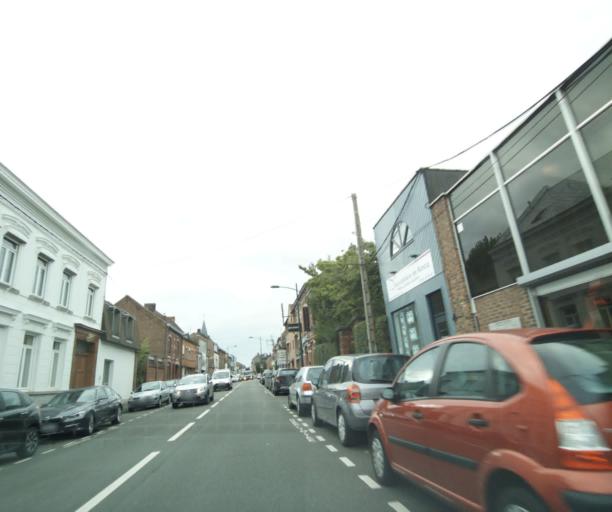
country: FR
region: Nord-Pas-de-Calais
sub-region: Departement du Nord
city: Roncq
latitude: 50.7552
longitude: 3.1207
